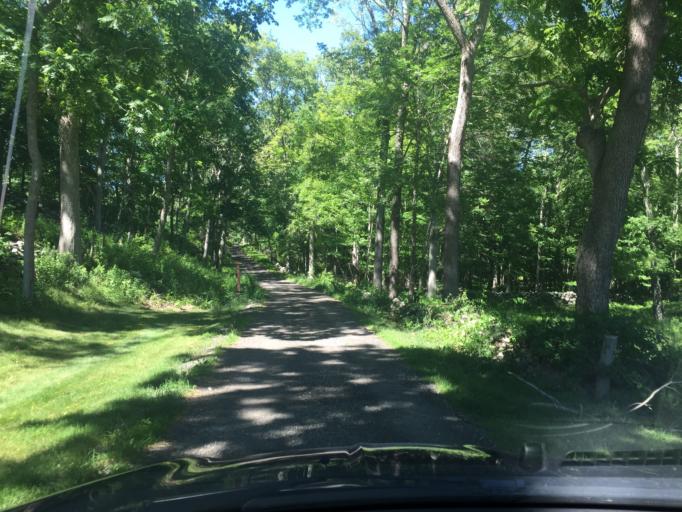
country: US
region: Rhode Island
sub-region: Washington County
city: Hopkinton
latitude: 41.5100
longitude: -71.8027
